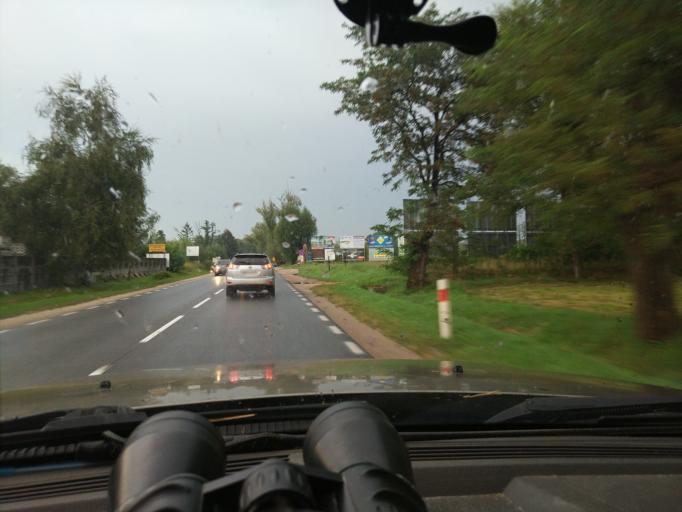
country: PL
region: Masovian Voivodeship
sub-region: Powiat pruszkowski
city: Otrebusy
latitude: 52.1405
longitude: 20.7712
